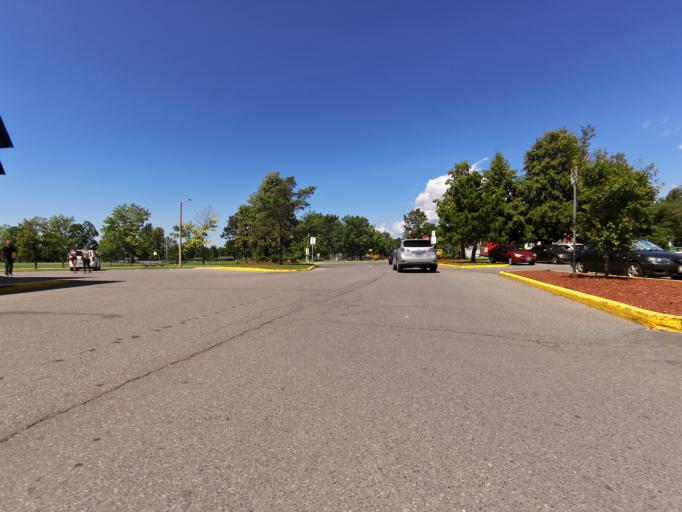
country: CA
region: Ontario
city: Ottawa
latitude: 45.3508
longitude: -75.6721
